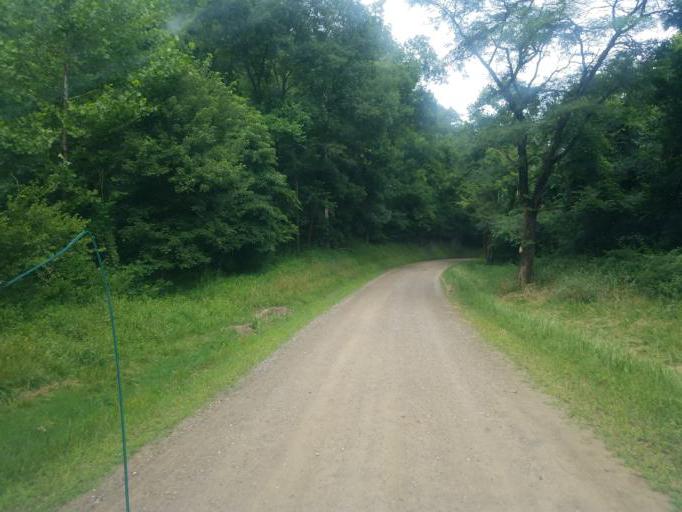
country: US
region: Ohio
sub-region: Knox County
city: Oak Hill
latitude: 40.4028
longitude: -82.1700
